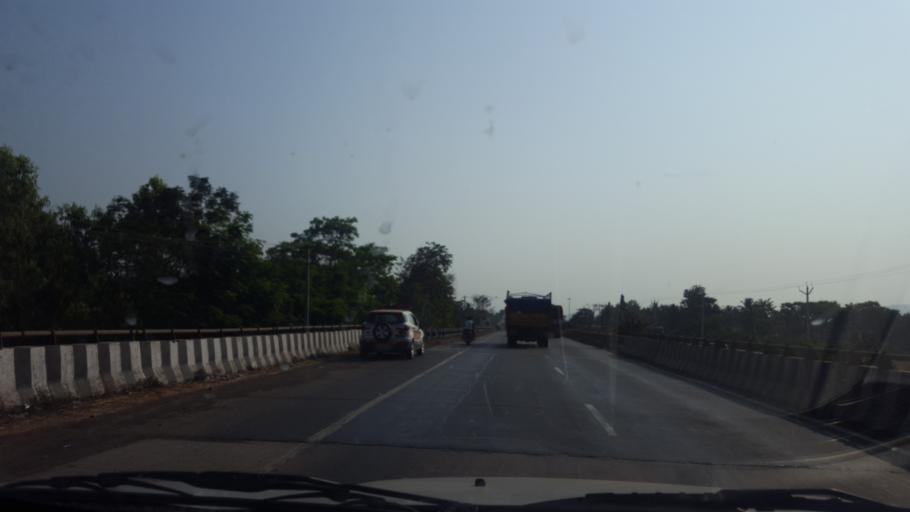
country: IN
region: Andhra Pradesh
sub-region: Vishakhapatnam
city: Elamanchili
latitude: 17.5910
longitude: 82.8706
